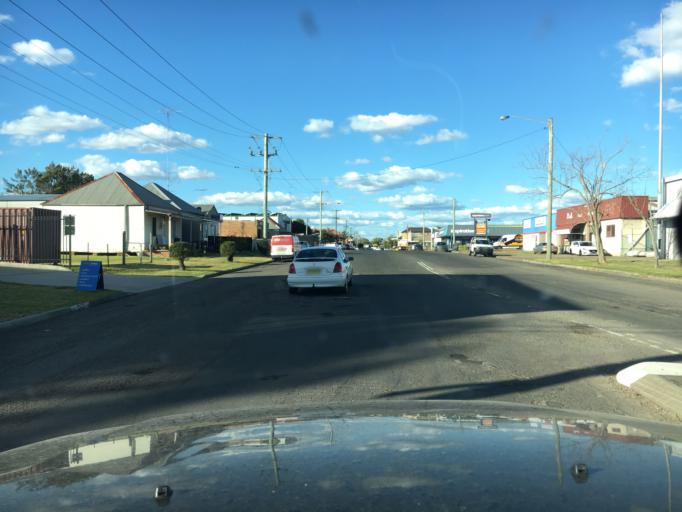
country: AU
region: New South Wales
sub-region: Maitland Municipality
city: East Maitland
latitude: -32.7482
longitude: 151.5789
